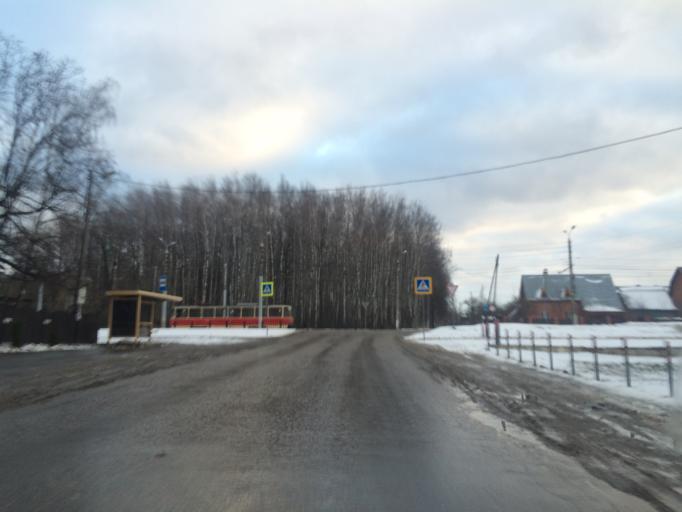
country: RU
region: Tula
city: Tula
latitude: 54.2198
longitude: 37.7040
